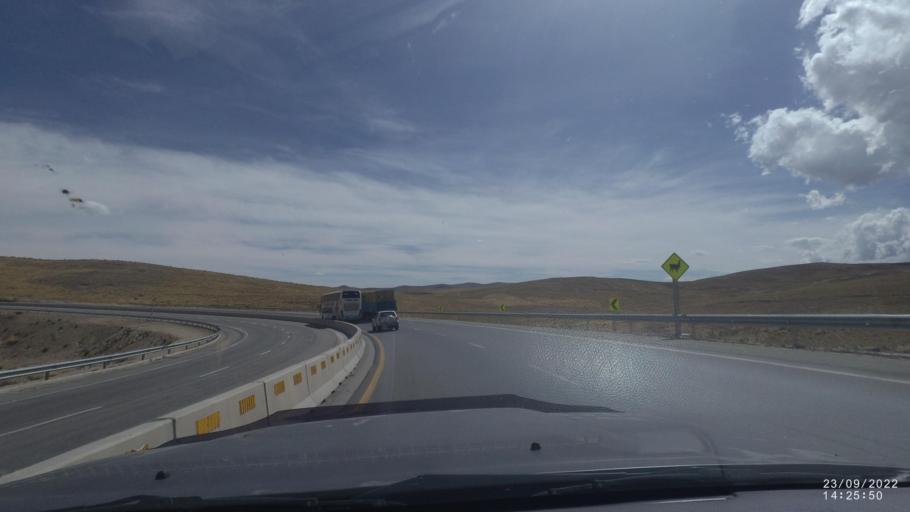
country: BO
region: Cochabamba
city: Colchani
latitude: -17.6648
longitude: -66.7581
